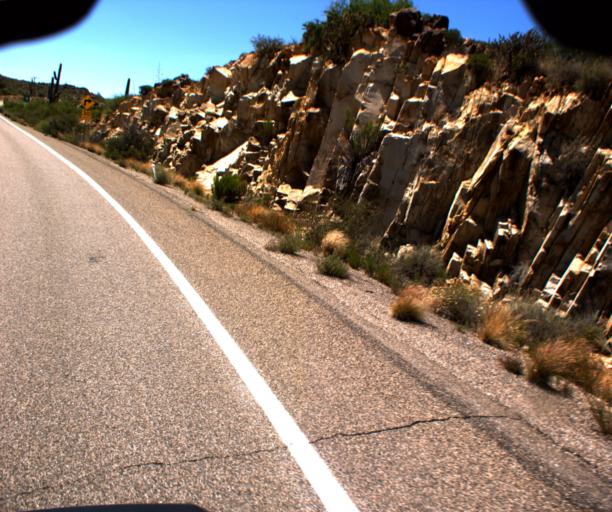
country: US
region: Arizona
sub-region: Yavapai County
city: Bagdad
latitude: 34.5249
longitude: -113.1241
